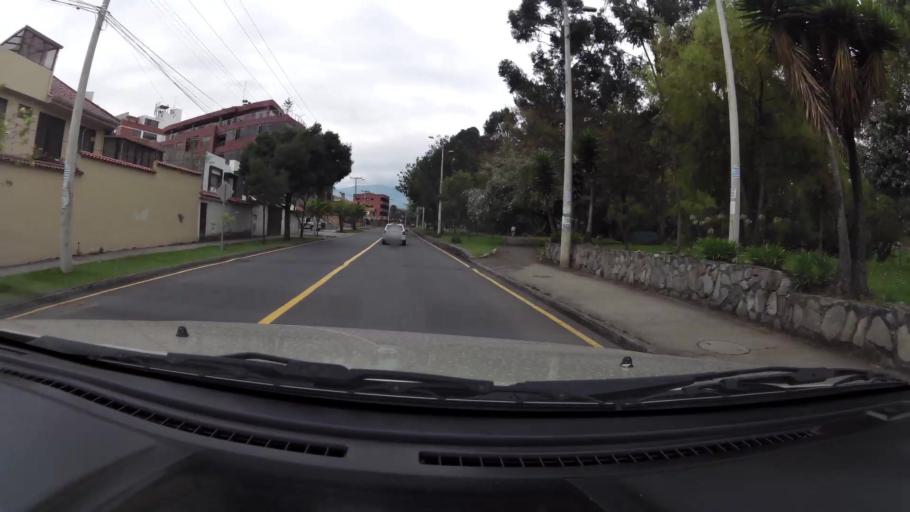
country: EC
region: Azuay
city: Cuenca
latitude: -2.9108
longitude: -79.0148
